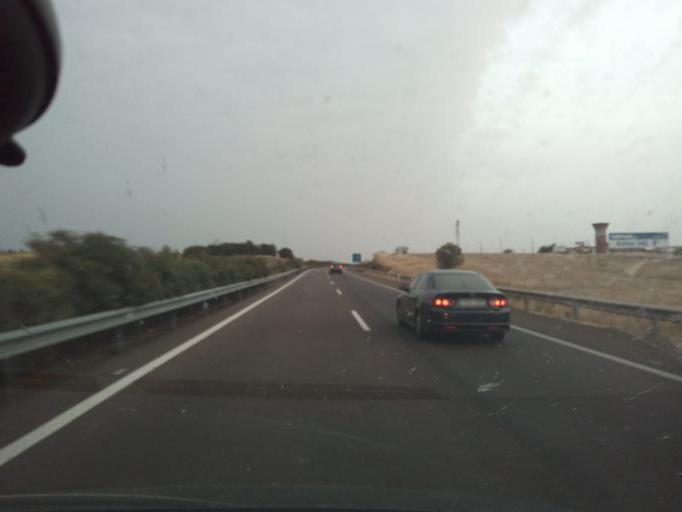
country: ES
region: Extremadura
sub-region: Provincia de Badajoz
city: Trujillanos
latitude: 38.9498
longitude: -6.2544
